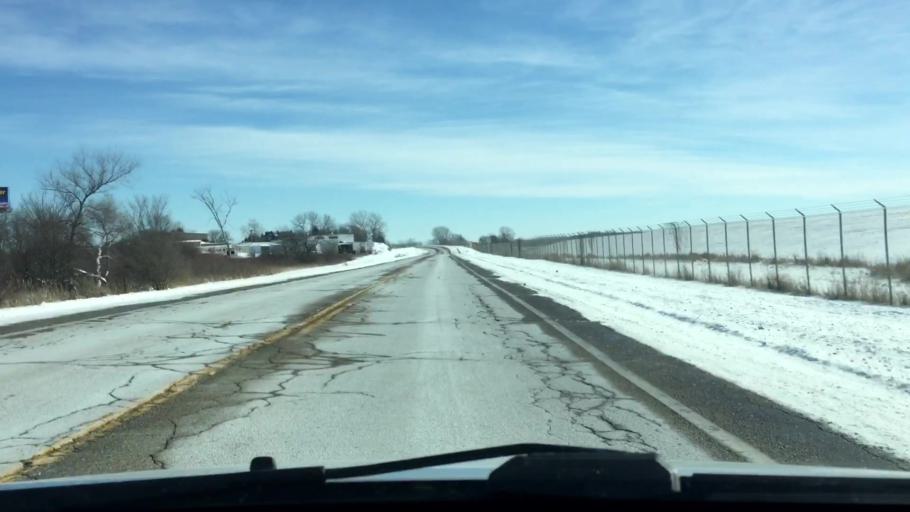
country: US
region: Wisconsin
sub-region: Waukesha County
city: Pewaukee
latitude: 43.0454
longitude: -88.2489
